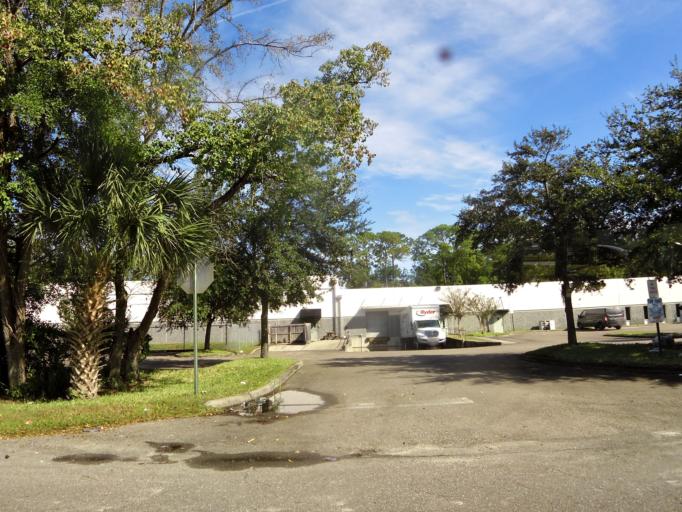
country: US
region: Florida
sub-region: Duval County
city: Jacksonville
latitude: 30.2653
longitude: -81.6126
